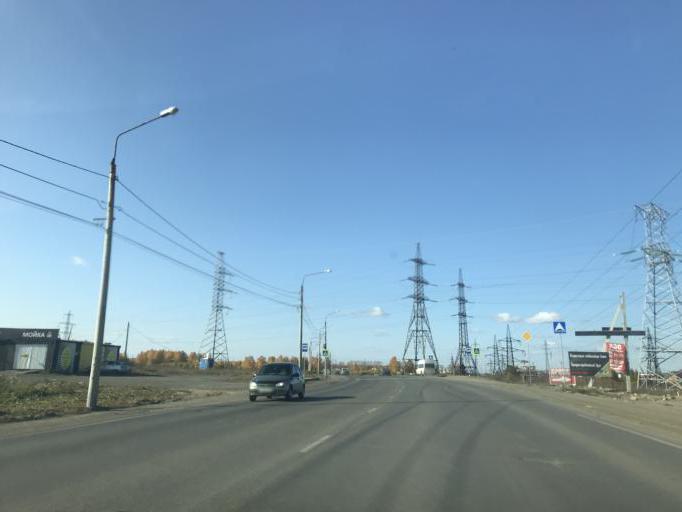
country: RU
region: Chelyabinsk
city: Roshchino
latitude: 55.2243
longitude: 61.2918
